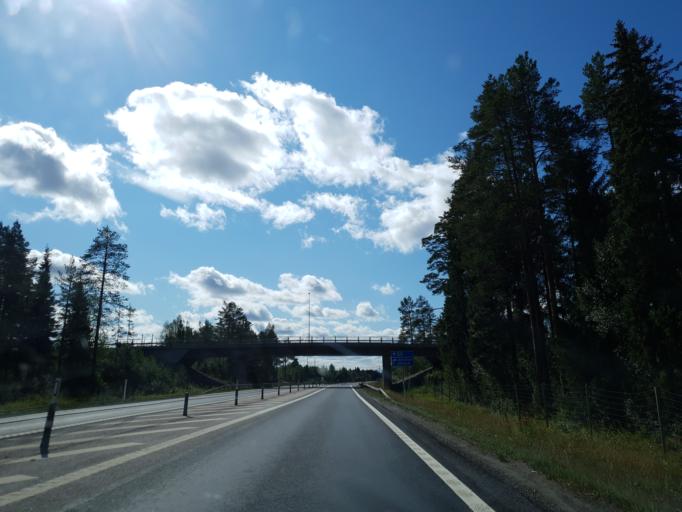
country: SE
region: Vaesterbotten
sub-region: Nordmalings Kommun
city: Nordmaling
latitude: 63.5376
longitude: 19.4031
